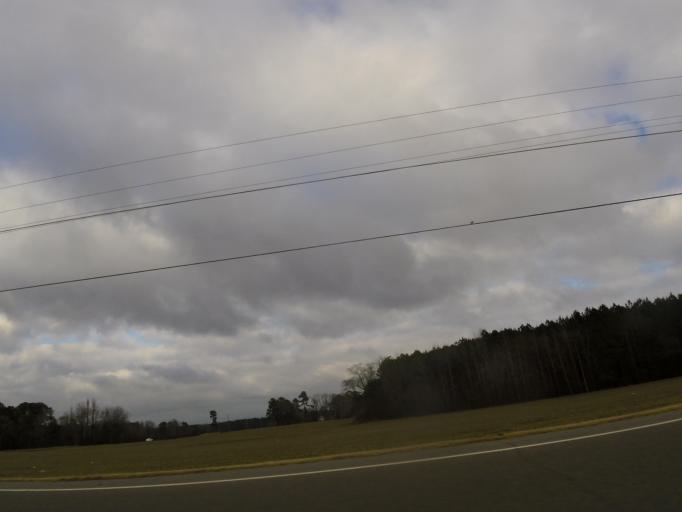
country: US
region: North Carolina
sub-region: Edgecombe County
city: Pinetops
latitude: 35.7987
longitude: -77.6365
